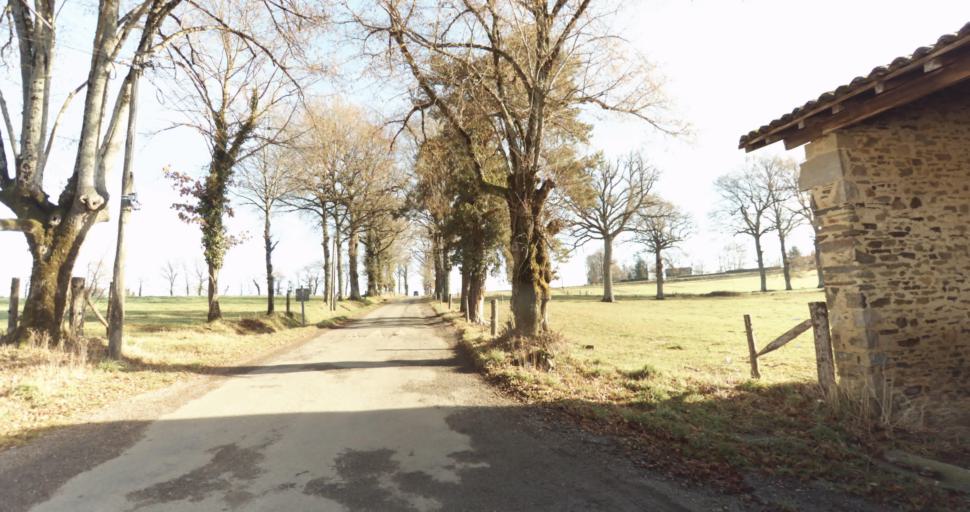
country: FR
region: Limousin
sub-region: Departement de la Haute-Vienne
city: Aixe-sur-Vienne
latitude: 45.7826
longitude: 1.1167
